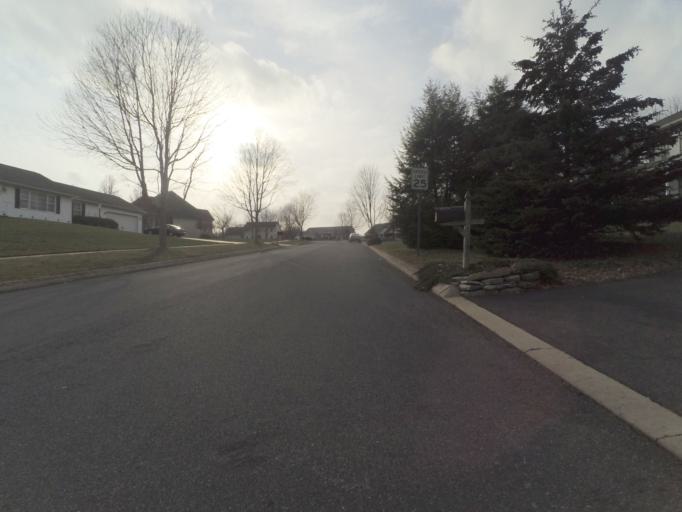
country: US
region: Pennsylvania
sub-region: Centre County
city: Park Forest Village
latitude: 40.7892
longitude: -77.9009
